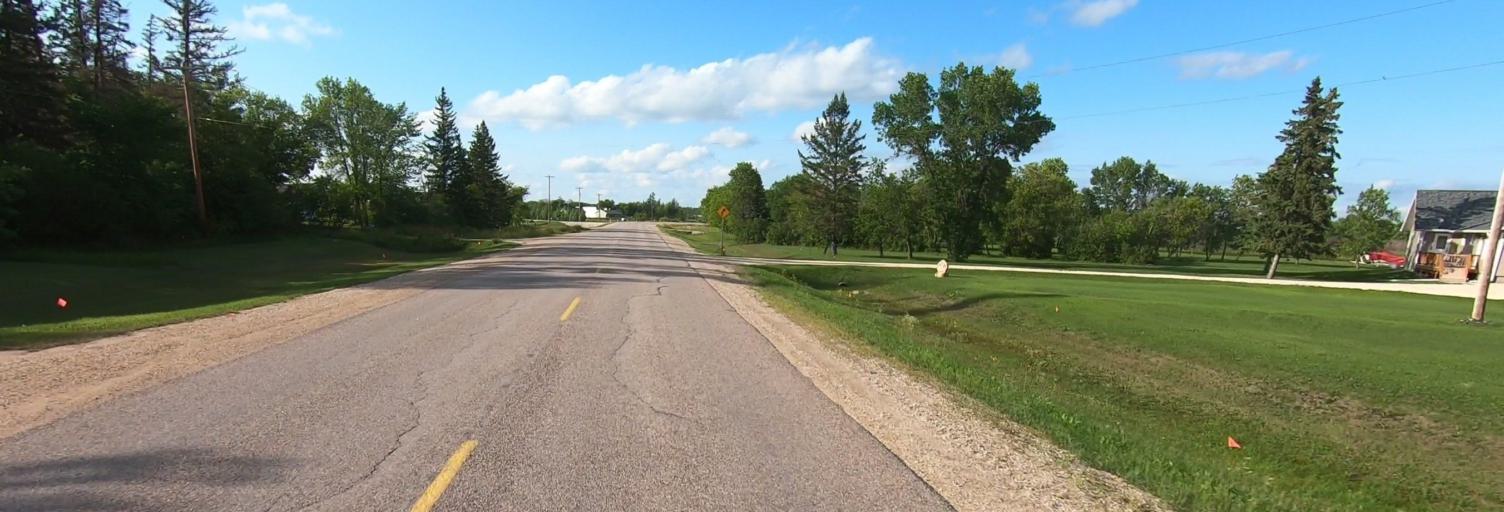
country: CA
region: Manitoba
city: Selkirk
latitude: 50.2093
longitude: -96.8408
